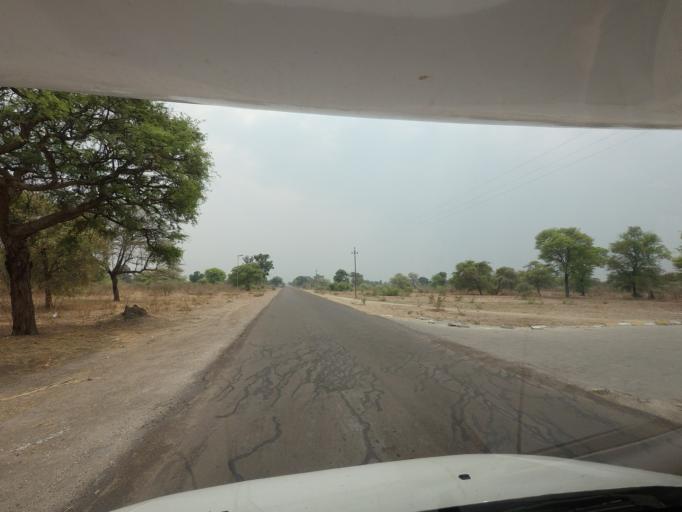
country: ZM
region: Western
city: Sesheke
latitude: -17.7258
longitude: 24.5270
